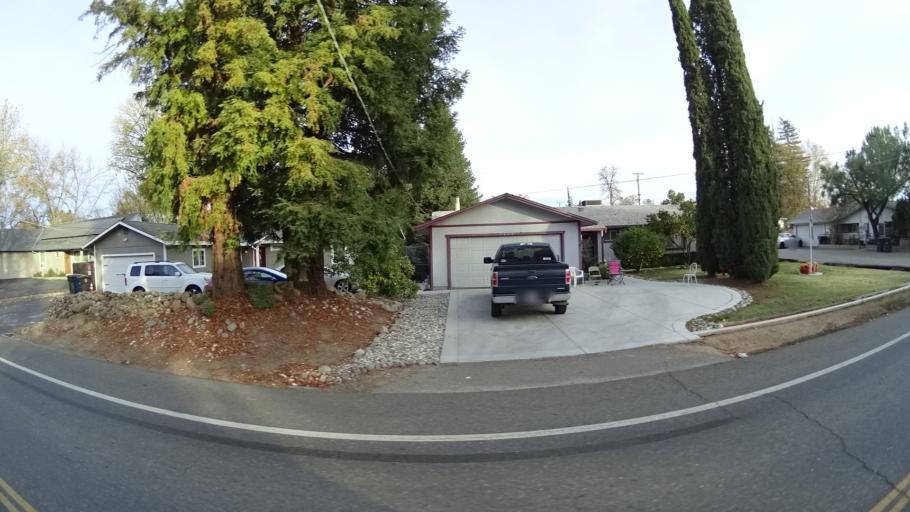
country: US
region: California
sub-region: Sacramento County
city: Citrus Heights
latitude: 38.7186
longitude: -121.2742
